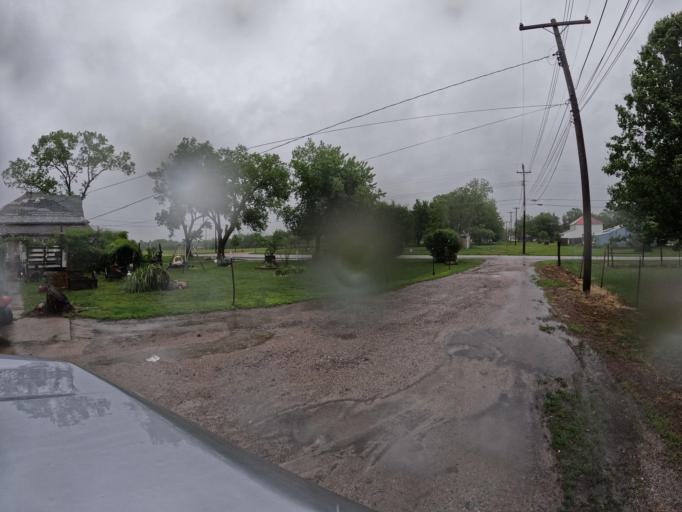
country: US
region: Nebraska
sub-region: Gage County
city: Wymore
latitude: 40.1426
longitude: -96.6656
